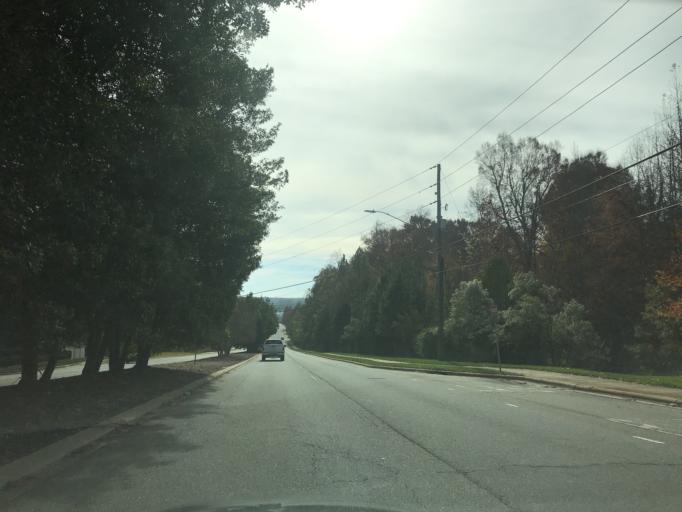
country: US
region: North Carolina
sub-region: Wake County
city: West Raleigh
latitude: 35.8507
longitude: -78.6805
